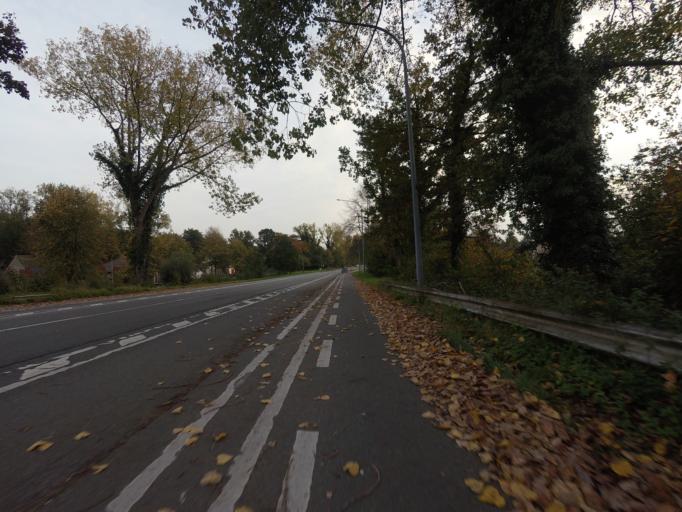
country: BE
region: Flanders
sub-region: Provincie Oost-Vlaanderen
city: Destelbergen
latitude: 51.0848
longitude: 3.7587
